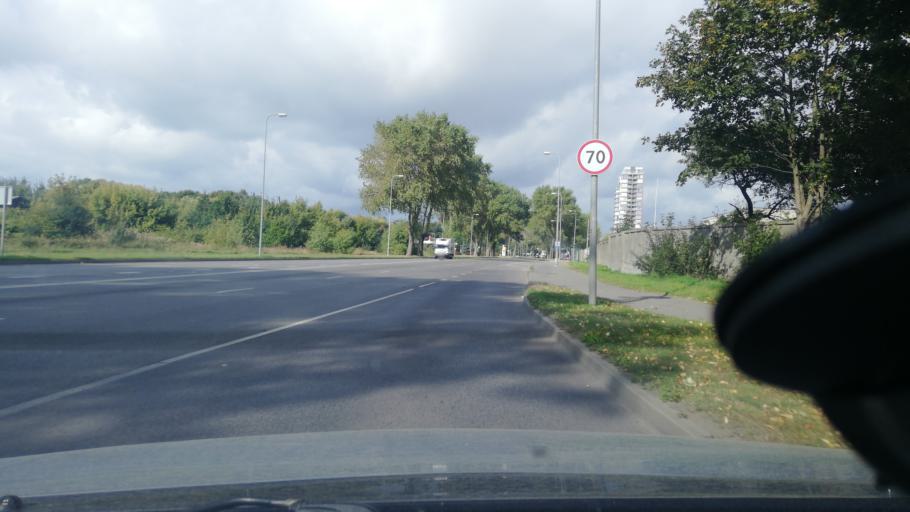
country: LT
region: Klaipedos apskritis
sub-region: Klaipeda
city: Klaipeda
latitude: 55.6671
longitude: 21.1620
